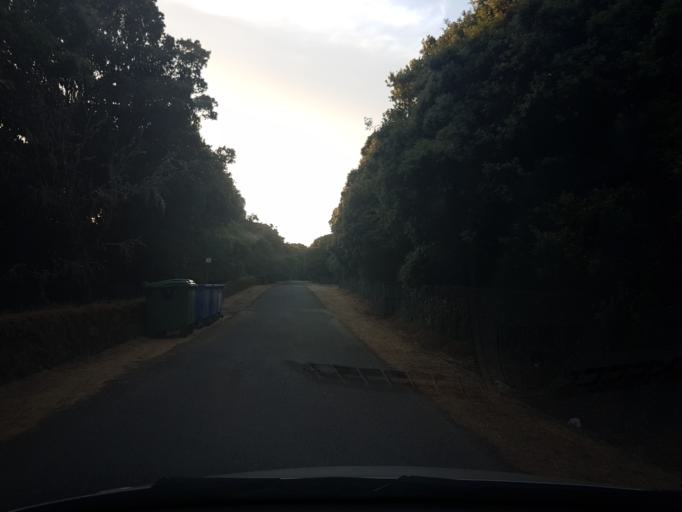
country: IT
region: Sardinia
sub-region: Provincia di Oristano
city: Seneghe
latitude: 40.1144
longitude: 8.5762
